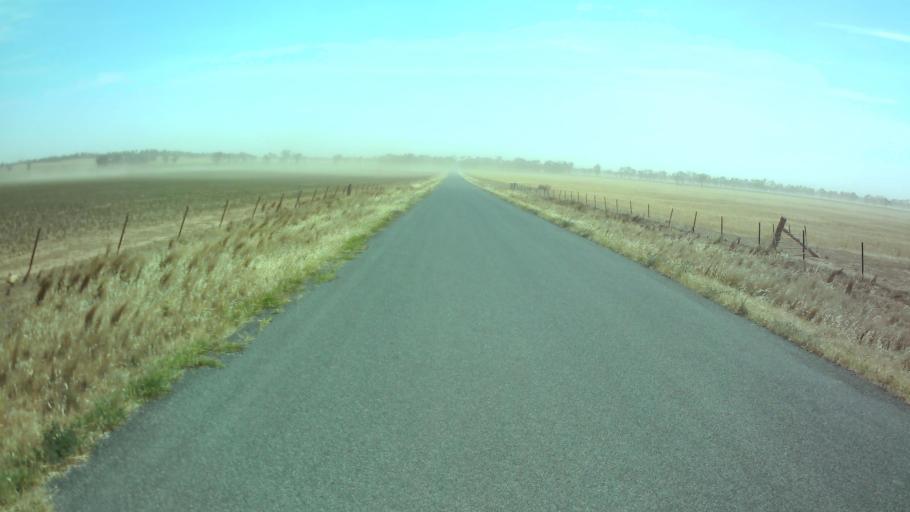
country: AU
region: New South Wales
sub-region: Weddin
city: Grenfell
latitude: -33.7283
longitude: 147.9984
